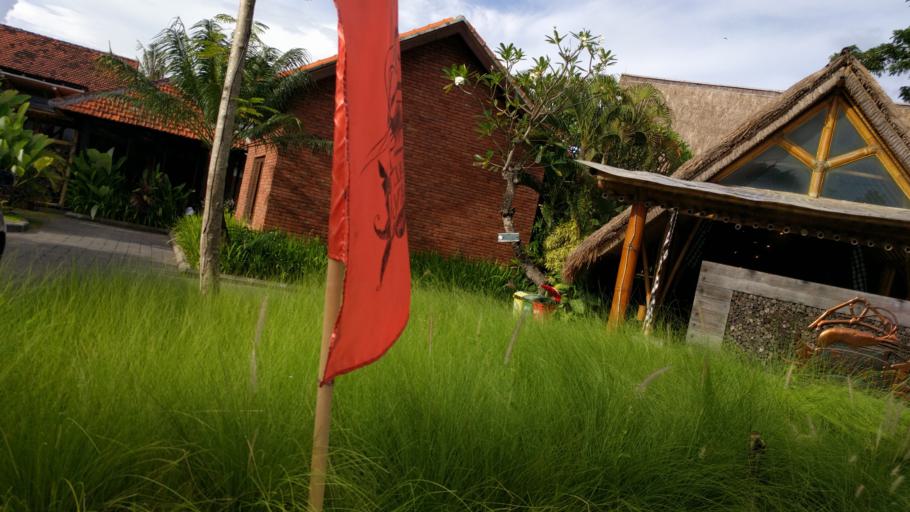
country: ID
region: Bali
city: Kuta
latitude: -8.7000
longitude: 115.1827
